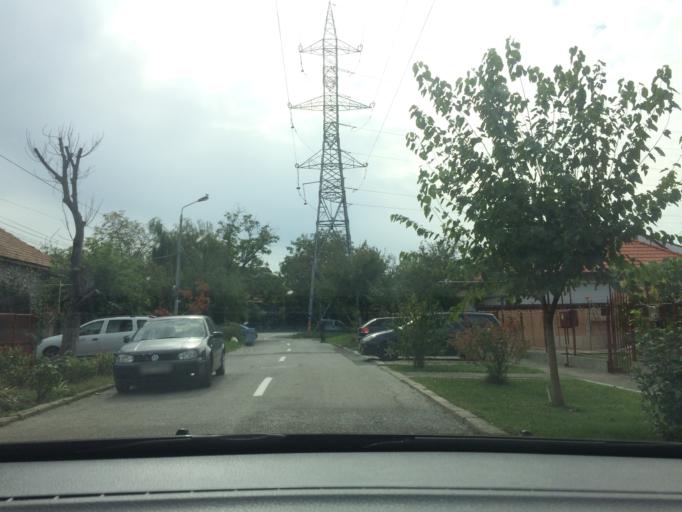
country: RO
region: Timis
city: Timisoara
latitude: 45.7544
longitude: 21.2082
